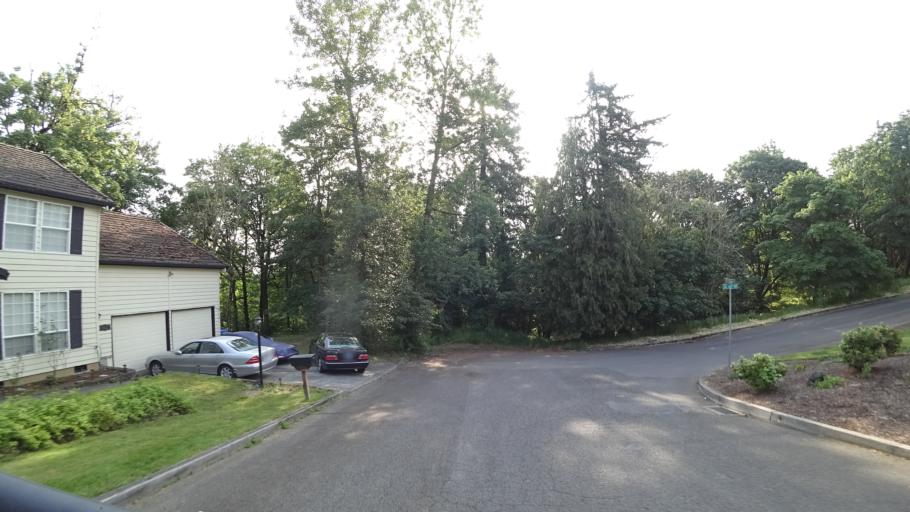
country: US
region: Oregon
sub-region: Clackamas County
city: Happy Valley
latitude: 45.4635
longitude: -122.5122
